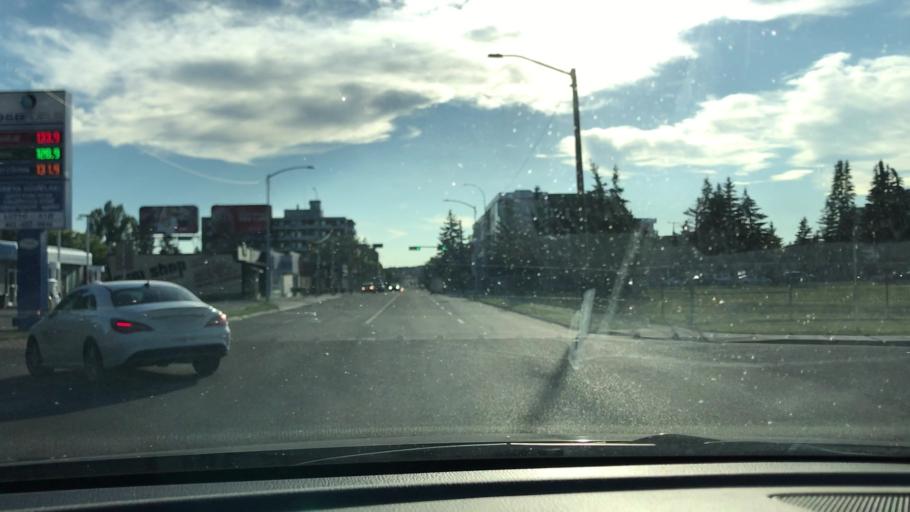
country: CA
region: Alberta
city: Calgary
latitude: 51.0378
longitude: -114.1221
